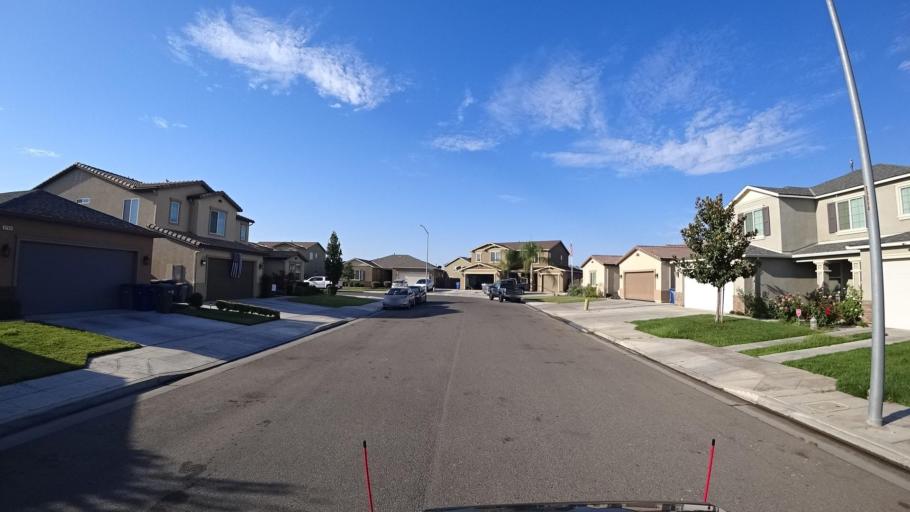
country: US
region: California
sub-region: Fresno County
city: Tarpey Village
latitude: 36.7904
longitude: -119.6708
